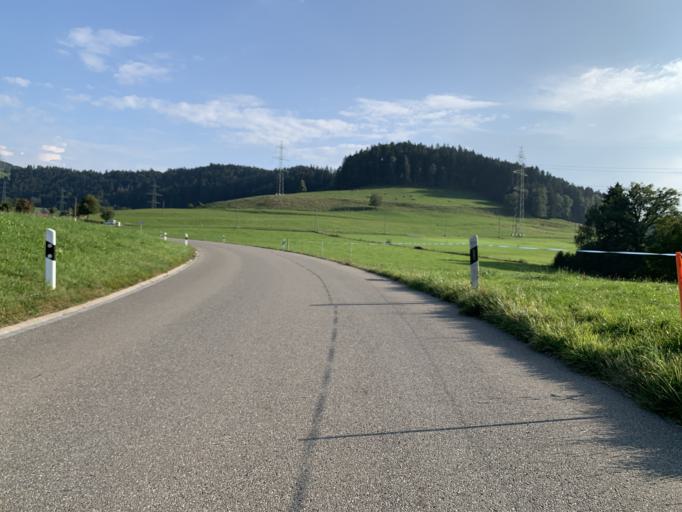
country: CH
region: Zurich
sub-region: Bezirk Hinwil
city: Baretswil
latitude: 47.3266
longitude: 8.8656
